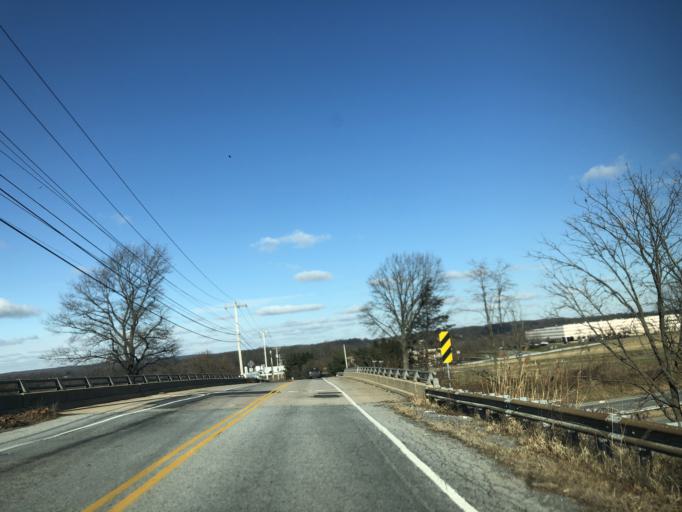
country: US
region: Pennsylvania
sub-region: Chester County
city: Coatesville
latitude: 39.9888
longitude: -75.8725
